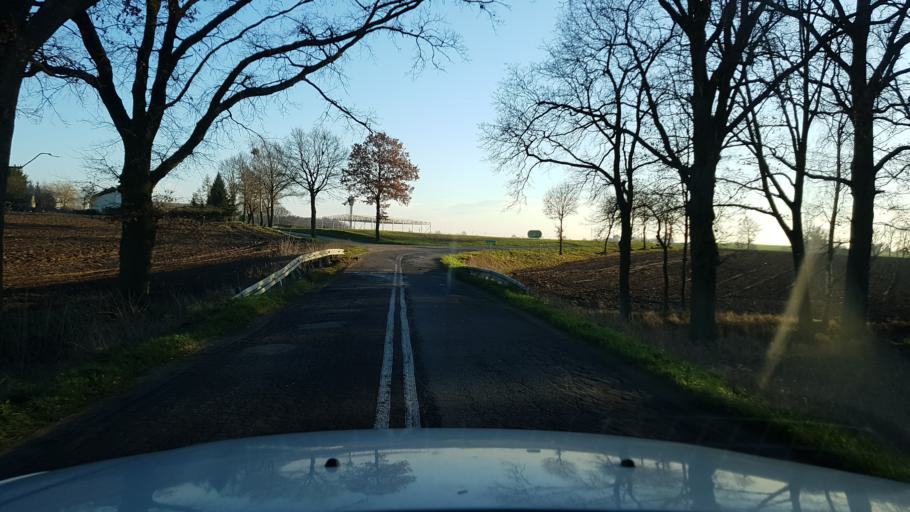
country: PL
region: West Pomeranian Voivodeship
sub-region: Powiat gryficki
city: Brojce
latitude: 53.9710
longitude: 15.3539
